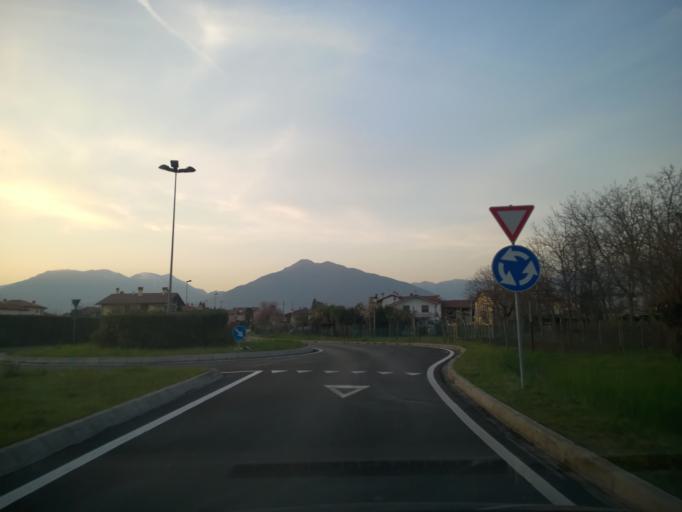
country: IT
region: Veneto
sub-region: Provincia di Vicenza
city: Marano Vicentino
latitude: 45.6896
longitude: 11.4448
